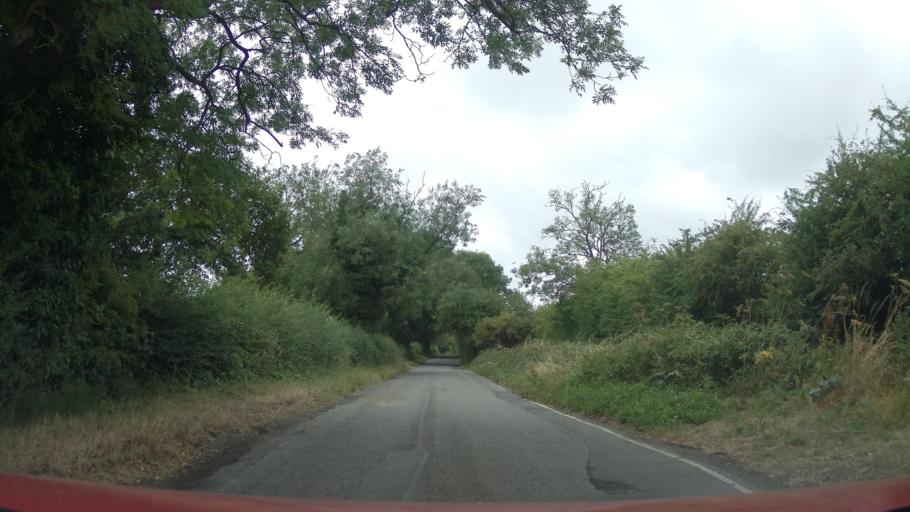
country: GB
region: England
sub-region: Derbyshire
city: Findern
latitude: 52.8874
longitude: -1.5233
